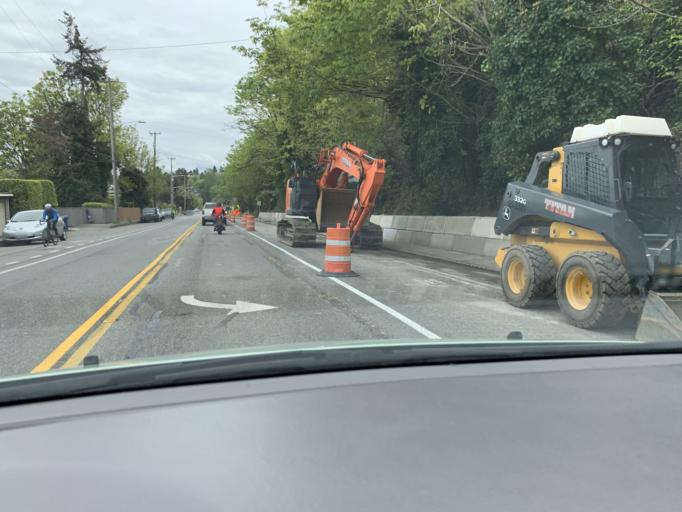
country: US
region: Washington
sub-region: King County
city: Bryn Mawr-Skyway
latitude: 47.5147
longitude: -122.2524
